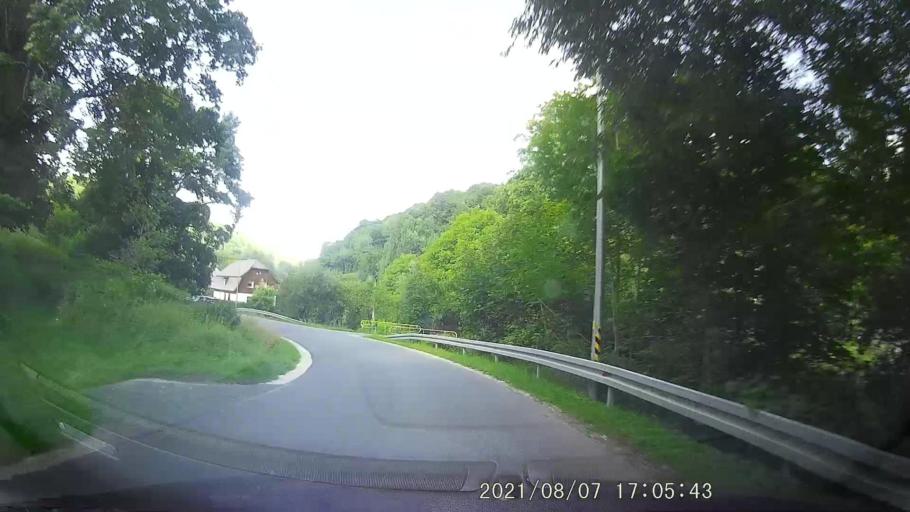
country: PL
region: Lower Silesian Voivodeship
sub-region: Powiat klodzki
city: Bystrzyca Klodzka
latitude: 50.2958
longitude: 16.5809
